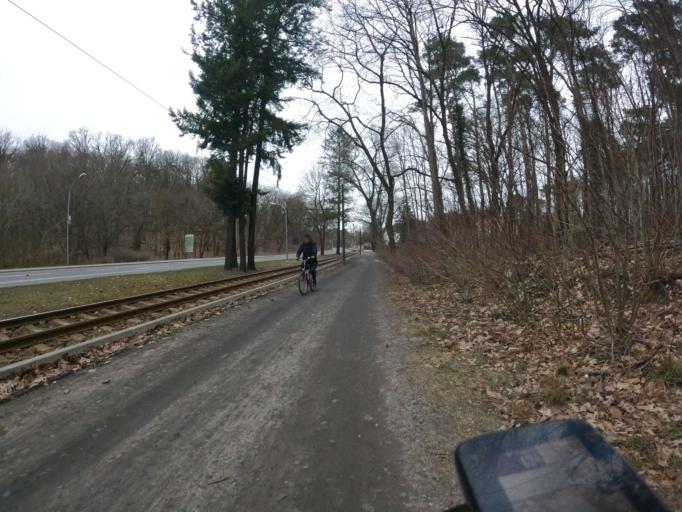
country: DE
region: Brandenburg
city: Strausberg
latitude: 52.5591
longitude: 13.8663
